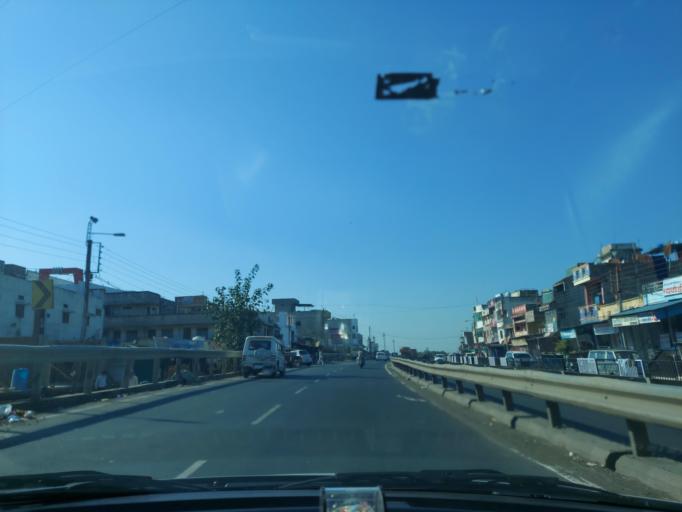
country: IN
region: Madhya Pradesh
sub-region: Dhar
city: Dhar
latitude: 22.7971
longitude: 75.2839
